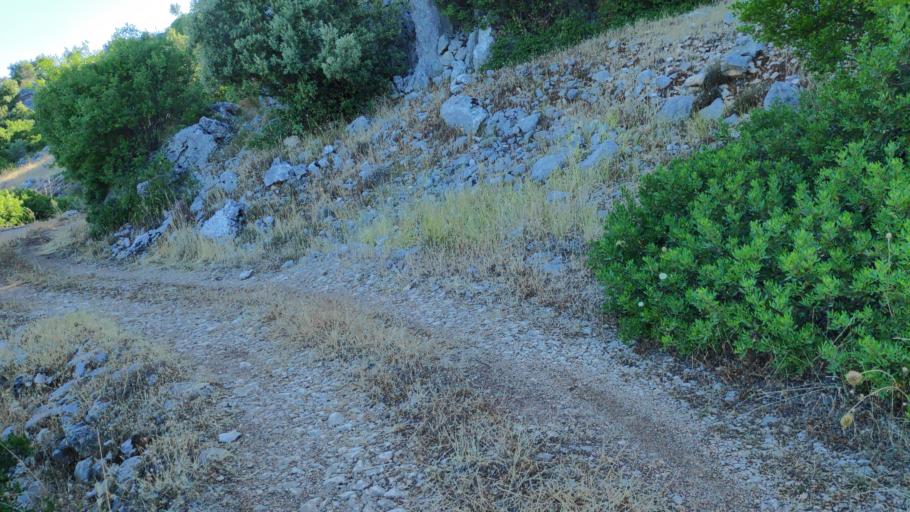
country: IT
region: Calabria
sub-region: Provincia di Reggio Calabria
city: Pazzano
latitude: 38.4575
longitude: 16.4364
